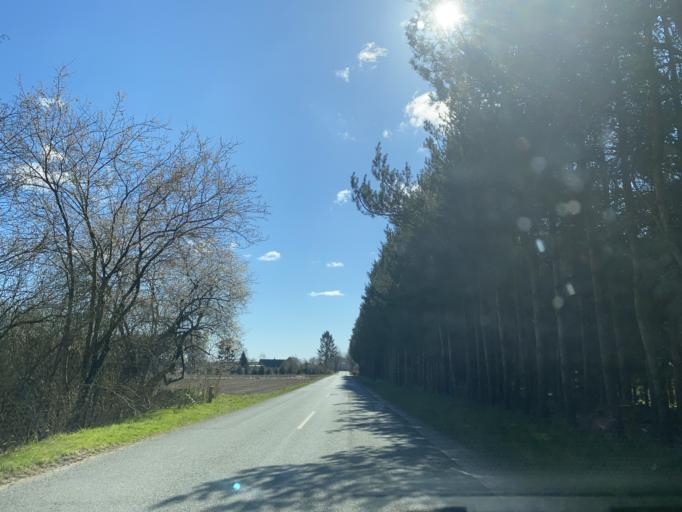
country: DK
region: Central Jutland
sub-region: Silkeborg Kommune
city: Svejbaek
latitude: 56.2415
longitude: 9.6615
